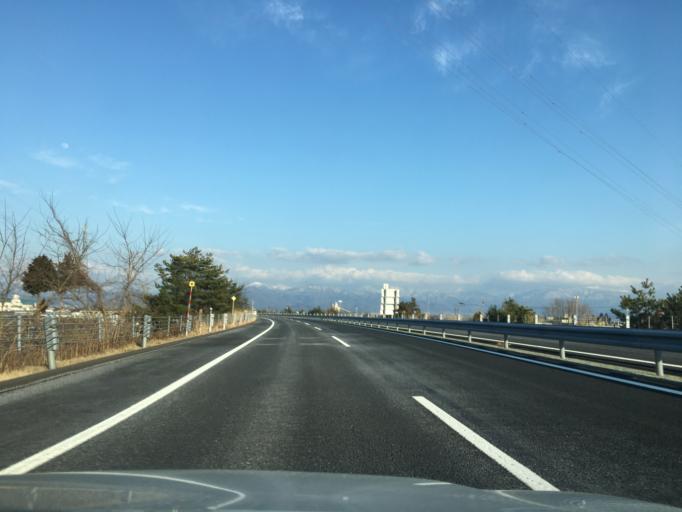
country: JP
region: Yamagata
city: Sagae
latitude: 38.3633
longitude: 140.2718
